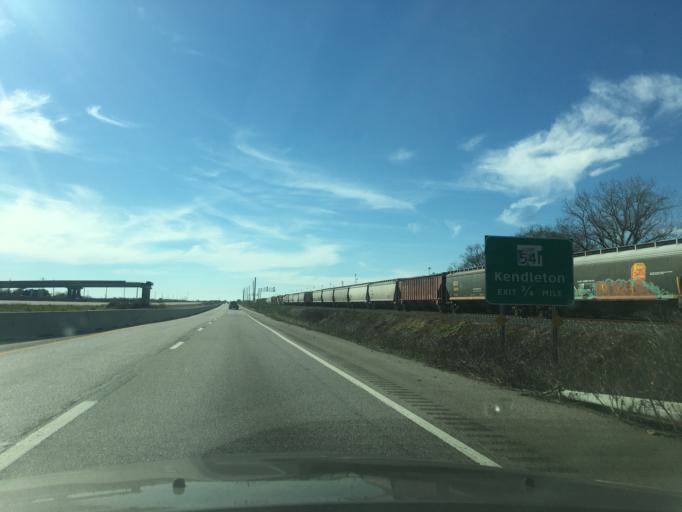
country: US
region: Texas
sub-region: Wharton County
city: East Bernard
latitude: 29.4694
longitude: -95.9640
